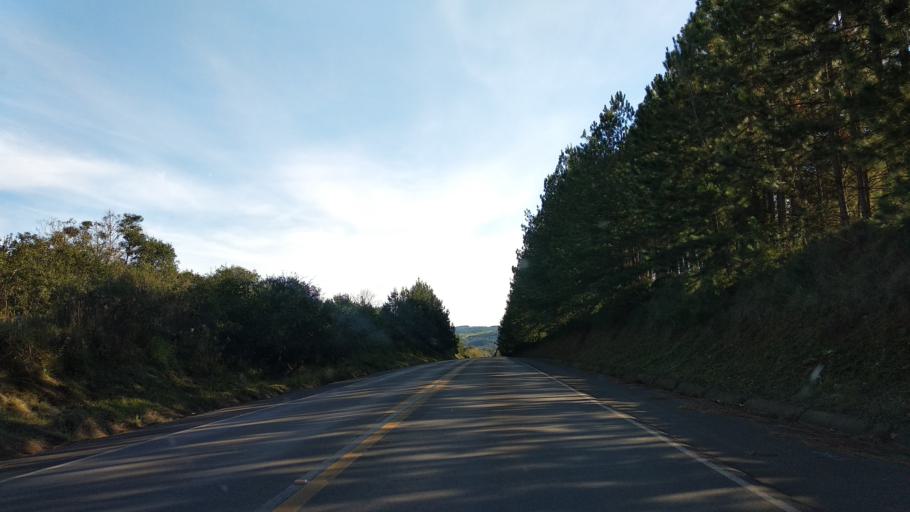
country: BR
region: Santa Catarina
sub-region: Celso Ramos
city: Celso Ramos
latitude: -27.5437
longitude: -51.4227
